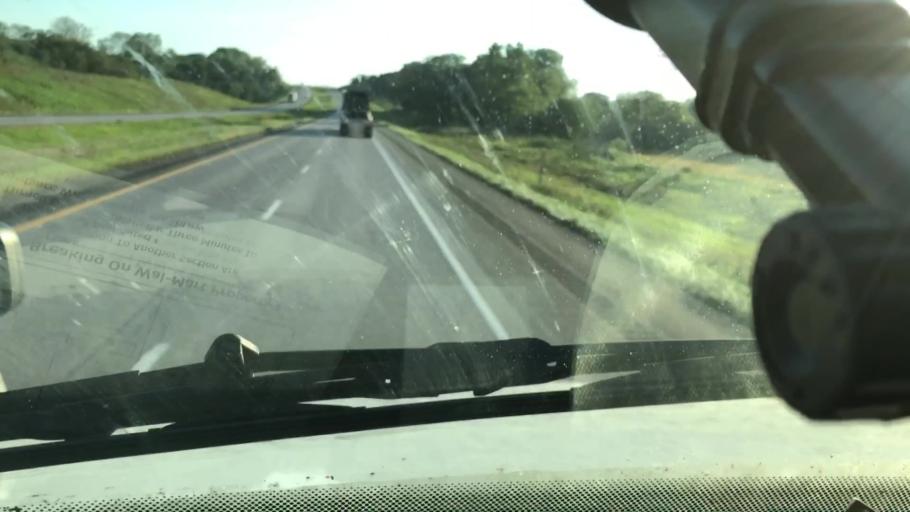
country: US
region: Iowa
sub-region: Pottawattamie County
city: Council Bluffs
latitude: 41.3321
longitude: -95.7414
